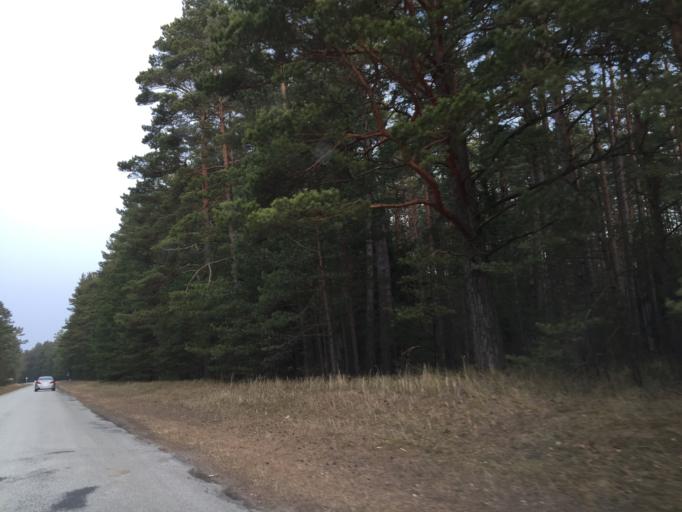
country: LV
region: Salacgrivas
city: Ainazi
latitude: 57.9364
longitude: 24.3918
